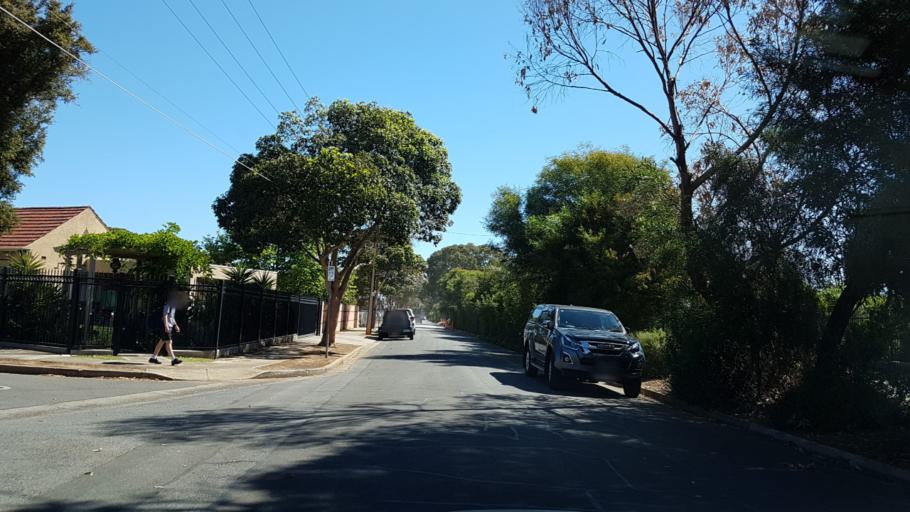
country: AU
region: South Australia
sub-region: Marion
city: South Plympton
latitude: -34.9653
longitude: 138.5588
